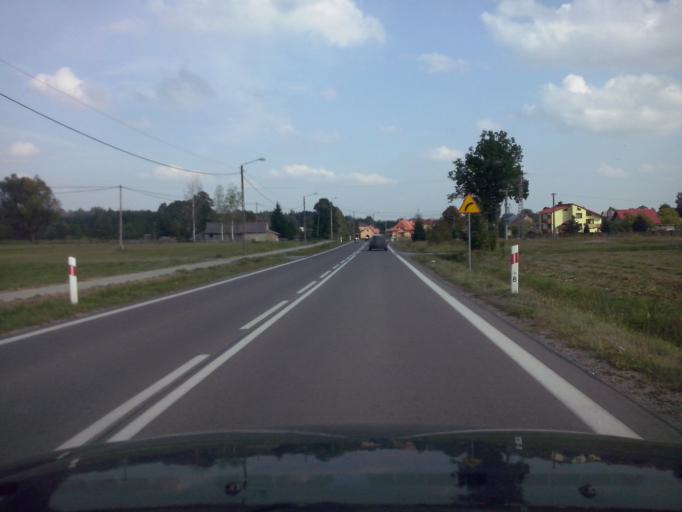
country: PL
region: Subcarpathian Voivodeship
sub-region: Powiat kolbuszowski
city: Niwiska
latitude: 50.2624
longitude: 21.6616
